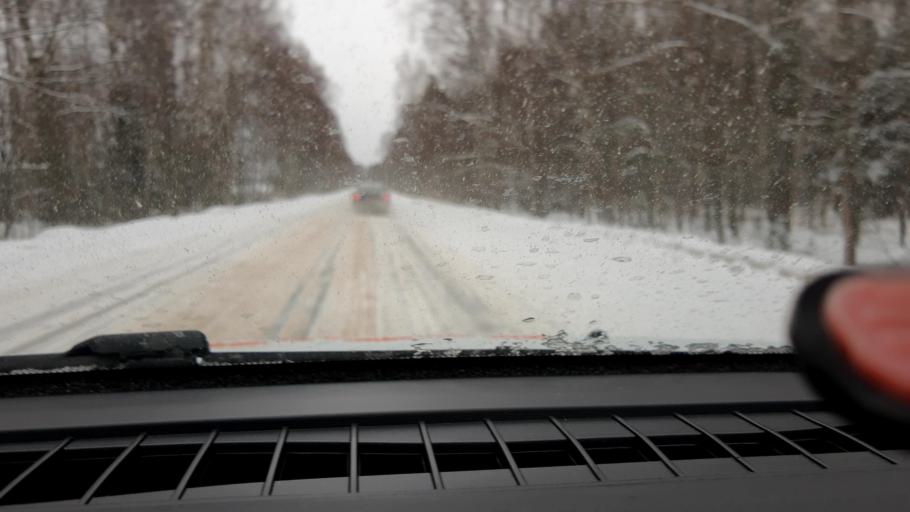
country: RU
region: Nizjnij Novgorod
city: Pamyat' Parizhskoy Kommuny
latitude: 56.2552
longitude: 44.4680
